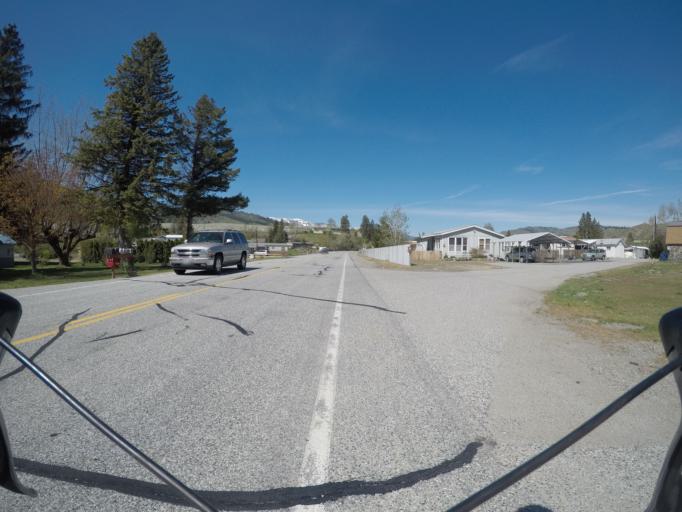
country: US
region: Washington
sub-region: Chelan County
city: Cashmere
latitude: 47.5311
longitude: -120.5454
